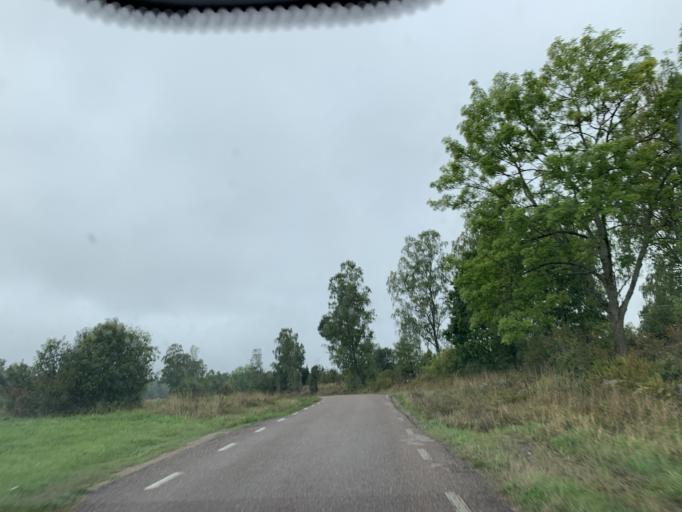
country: SE
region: Soedermanland
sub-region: Eskilstuna Kommun
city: Kvicksund
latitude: 59.5431
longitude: 16.3796
